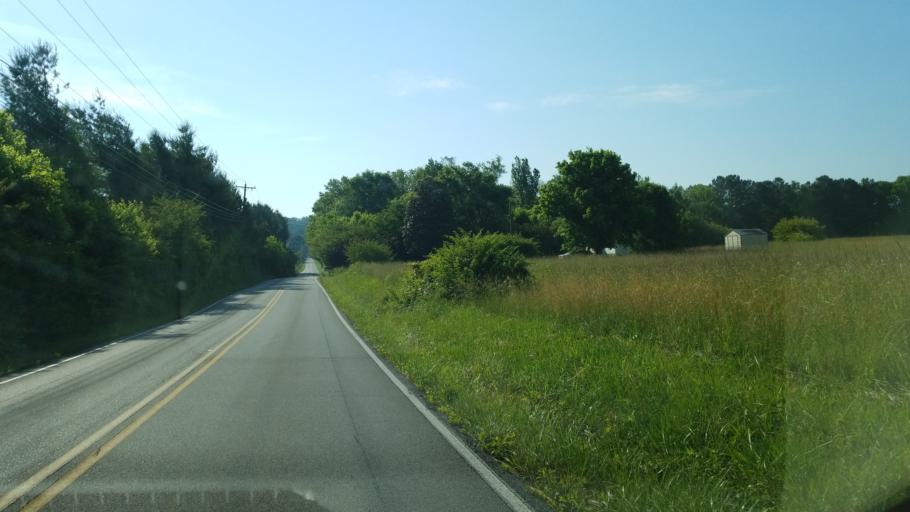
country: US
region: Tennessee
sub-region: Hamilton County
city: Collegedale
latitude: 35.0791
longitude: -85.0060
